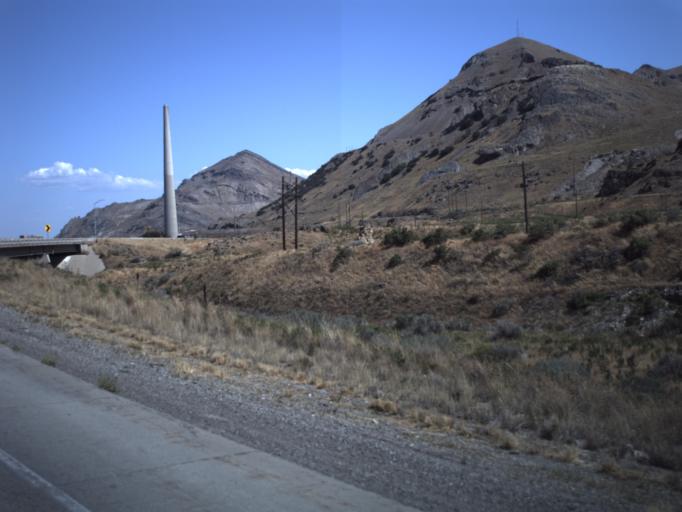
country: US
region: Utah
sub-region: Tooele County
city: Stansbury park
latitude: 40.7223
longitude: -112.2267
